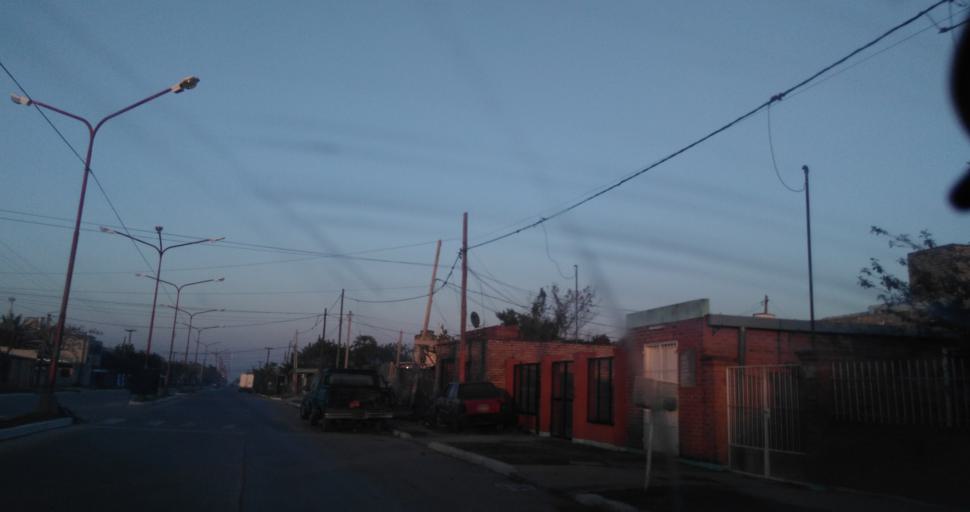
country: AR
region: Chaco
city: Resistencia
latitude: -27.4858
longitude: -58.9823
